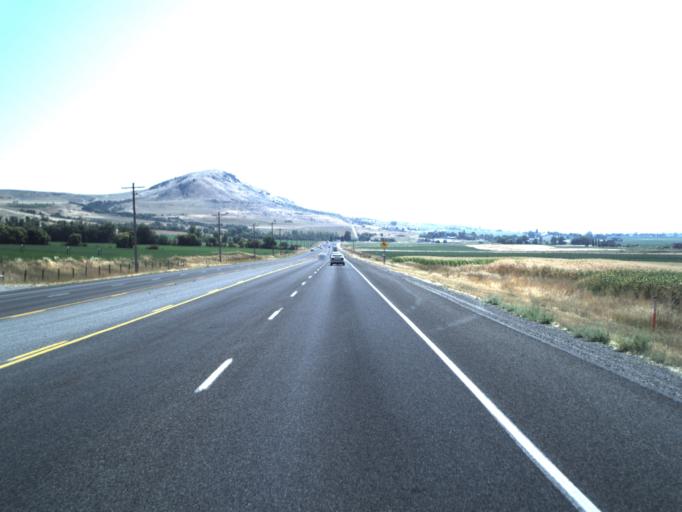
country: US
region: Utah
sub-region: Cache County
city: Richmond
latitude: 41.9058
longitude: -111.8148
